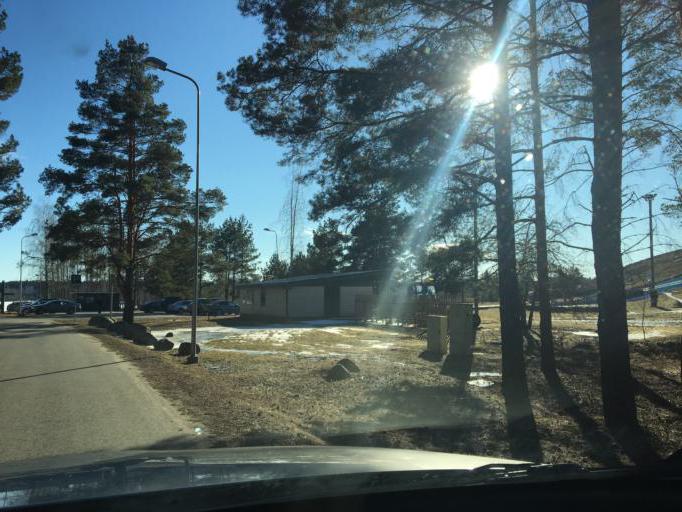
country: LV
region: Jekabpils Rajons
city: Jekabpils
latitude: 56.4832
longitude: 25.8522
